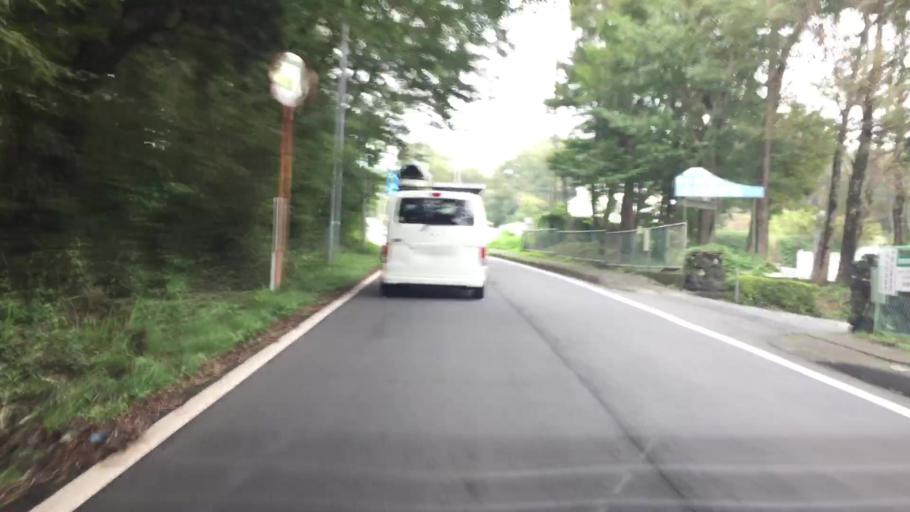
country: JP
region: Shizuoka
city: Fujinomiya
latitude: 35.3515
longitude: 138.5953
